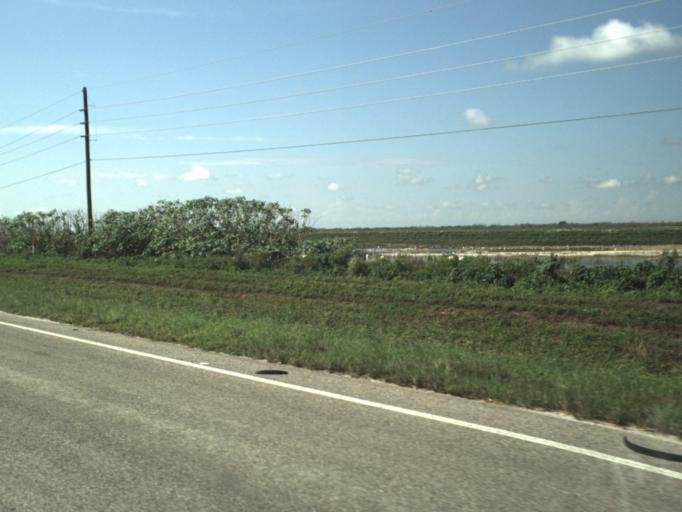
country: US
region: Florida
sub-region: Palm Beach County
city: Belle Glade Camp
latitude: 26.4290
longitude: -80.6108
